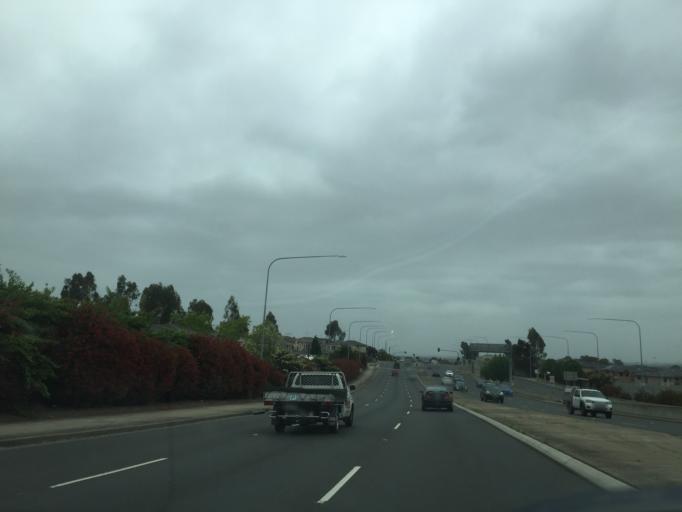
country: AU
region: New South Wales
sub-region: Blacktown
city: Stanhope Gardens
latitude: -33.7366
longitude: 150.9187
